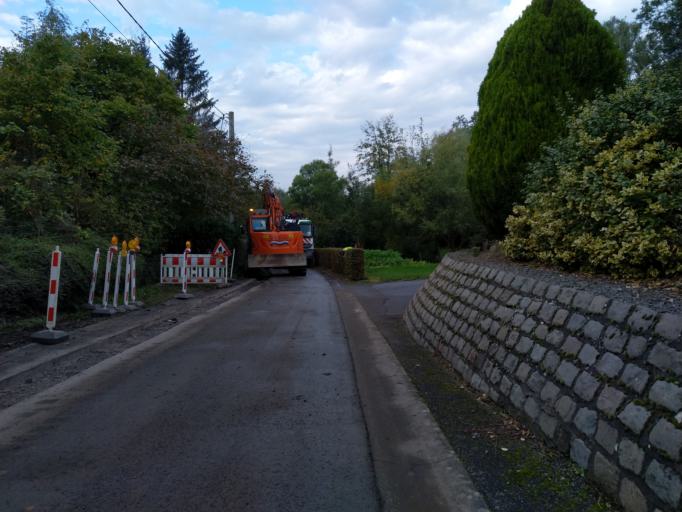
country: BE
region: Wallonia
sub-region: Province du Hainaut
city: Brugelette
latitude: 50.6076
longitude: 3.8340
